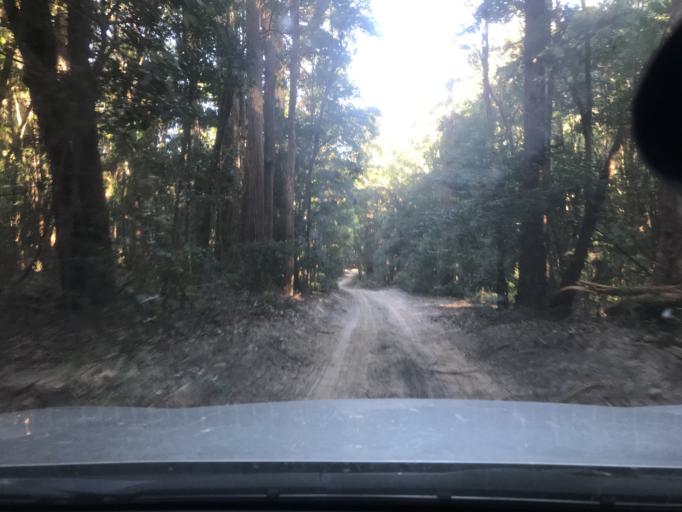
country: AU
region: Queensland
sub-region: Fraser Coast
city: Urangan
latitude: -25.3254
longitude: 153.1504
